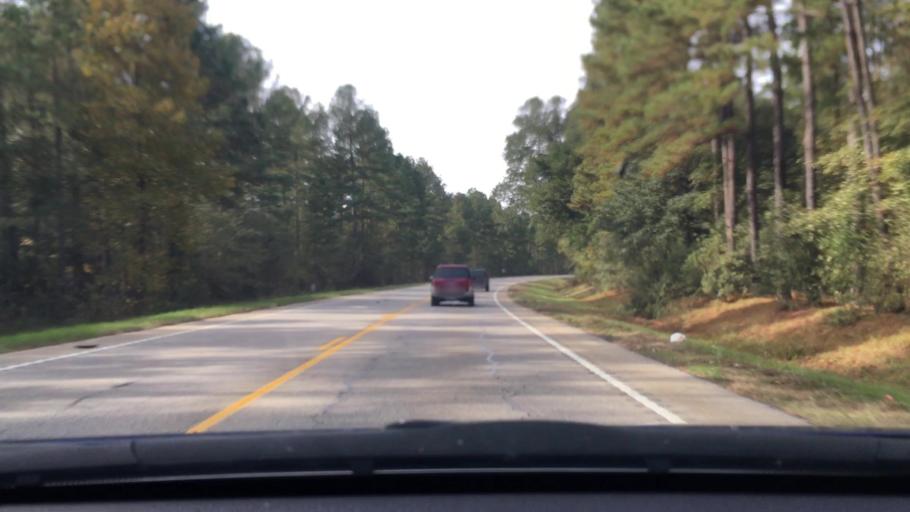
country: US
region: South Carolina
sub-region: Sumter County
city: Cherryvale
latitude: 33.9426
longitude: -80.4895
